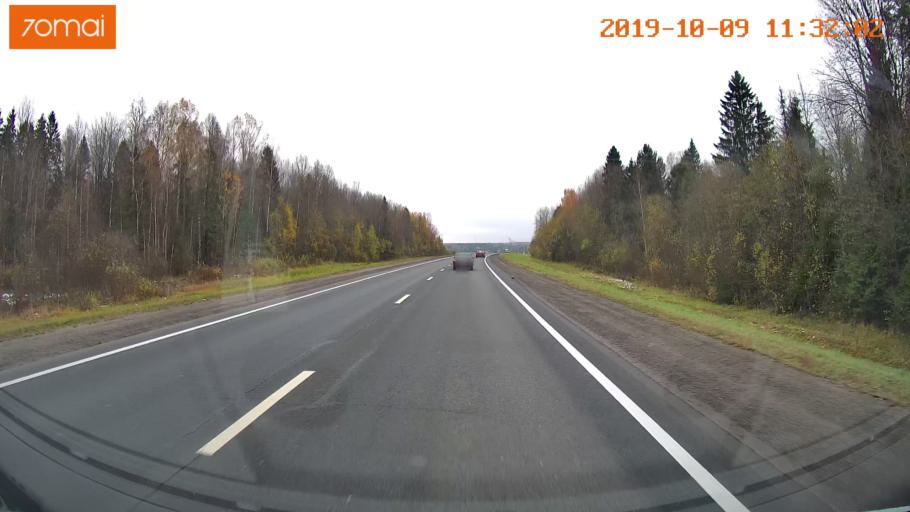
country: RU
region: Vologda
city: Gryazovets
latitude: 59.0399
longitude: 40.1049
